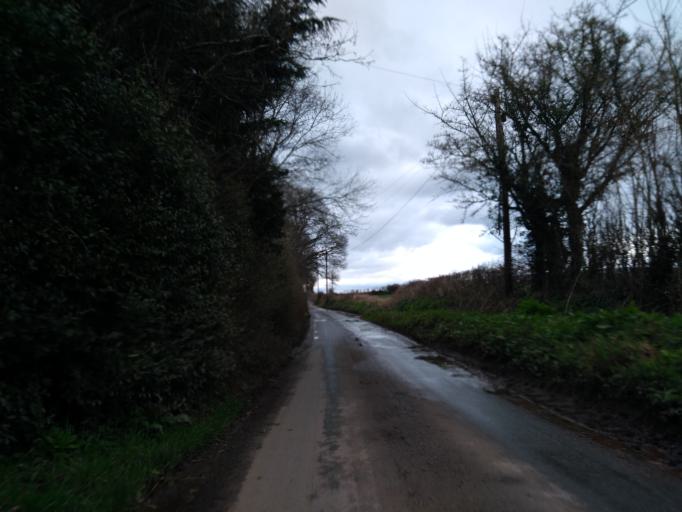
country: GB
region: England
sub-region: Devon
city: Crediton
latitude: 50.7840
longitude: -3.6056
